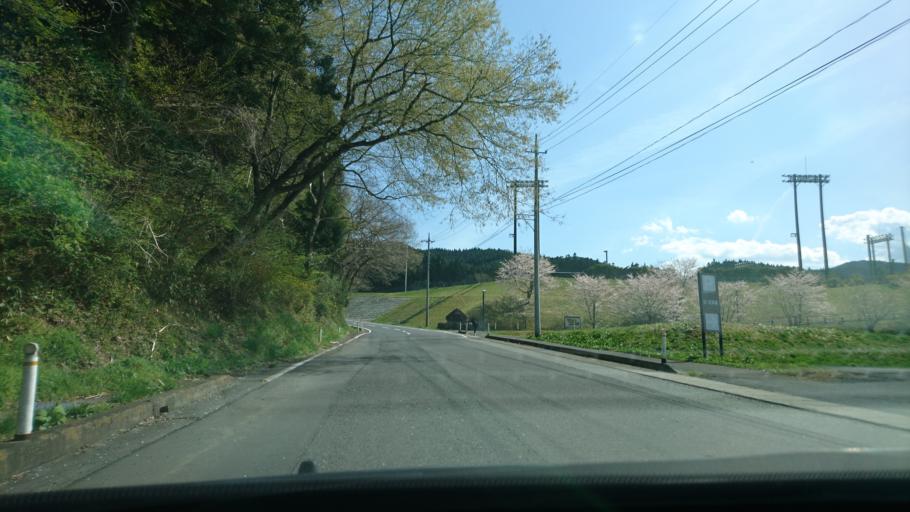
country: JP
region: Iwate
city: Ofunato
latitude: 38.9352
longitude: 141.4497
